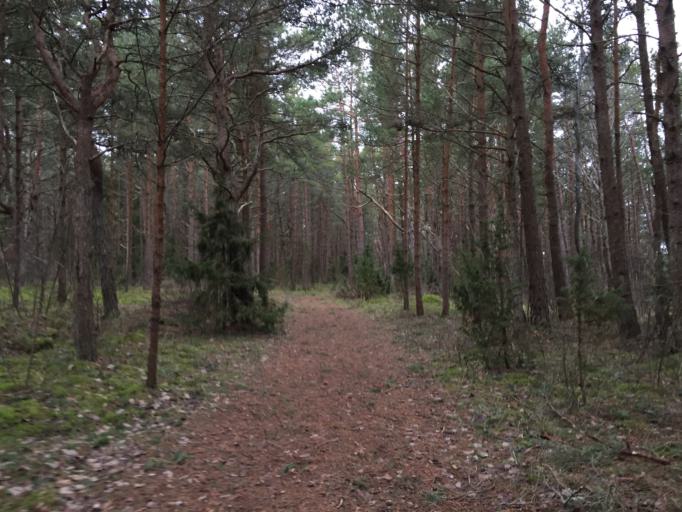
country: EE
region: Saare
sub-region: Kuressaare linn
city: Kuressaare
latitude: 58.5684
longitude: 22.2864
